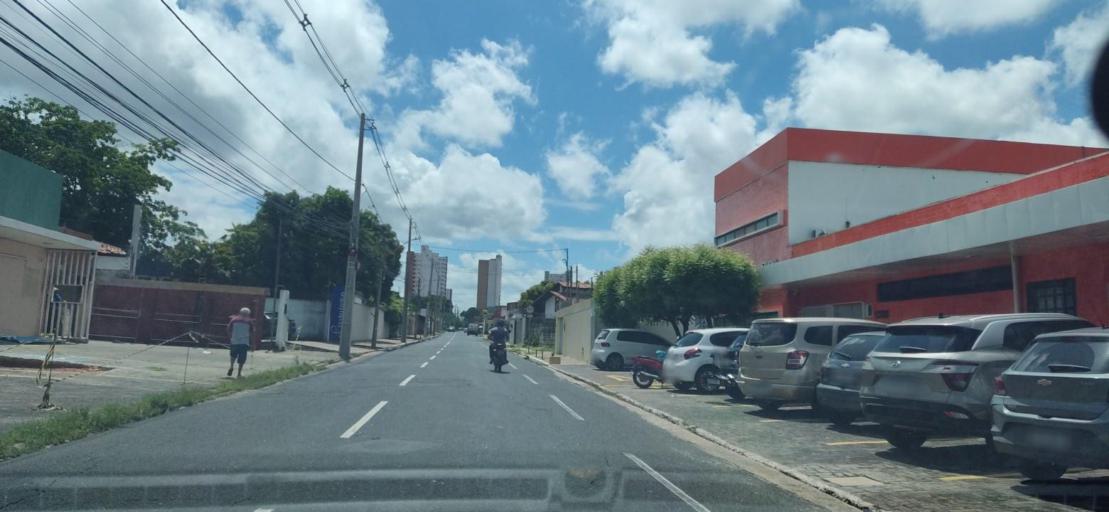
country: BR
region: Piaui
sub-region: Teresina
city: Teresina
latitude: -5.0636
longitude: -42.7922
